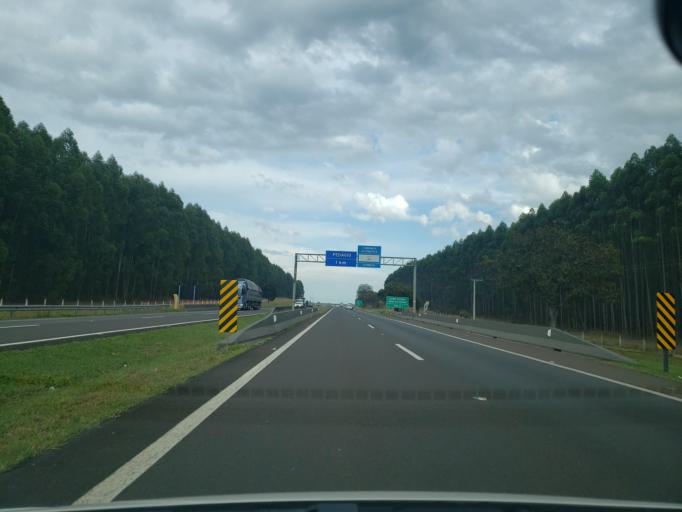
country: BR
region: Sao Paulo
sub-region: Itirapina
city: Itirapina
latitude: -22.2615
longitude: -47.8875
